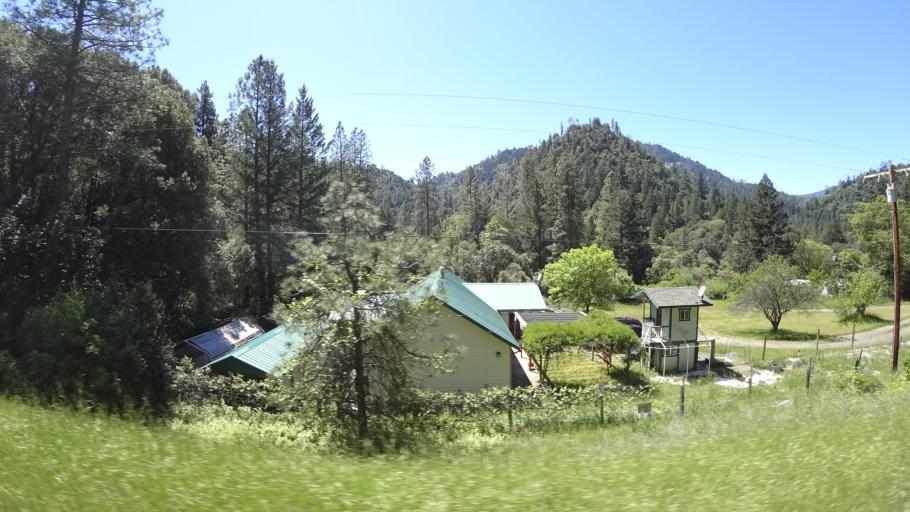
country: US
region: California
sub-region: Trinity County
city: Hayfork
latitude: 40.7807
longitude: -123.3328
